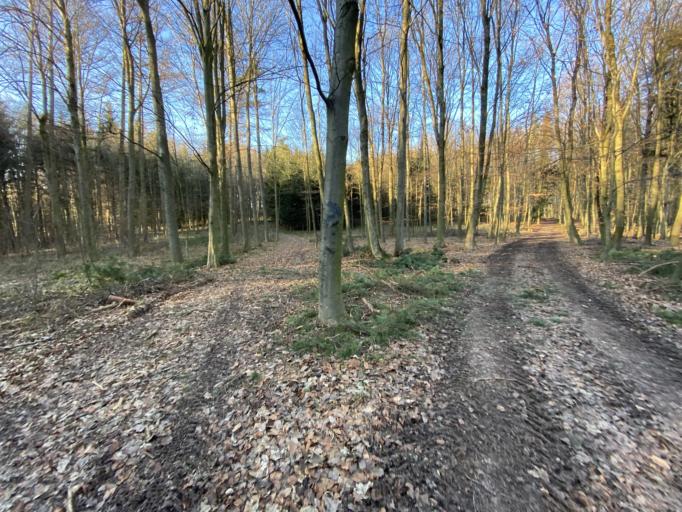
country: AT
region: Lower Austria
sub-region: Politischer Bezirk Sankt Polten
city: Boheimkirchen
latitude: 48.2058
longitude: 15.7279
